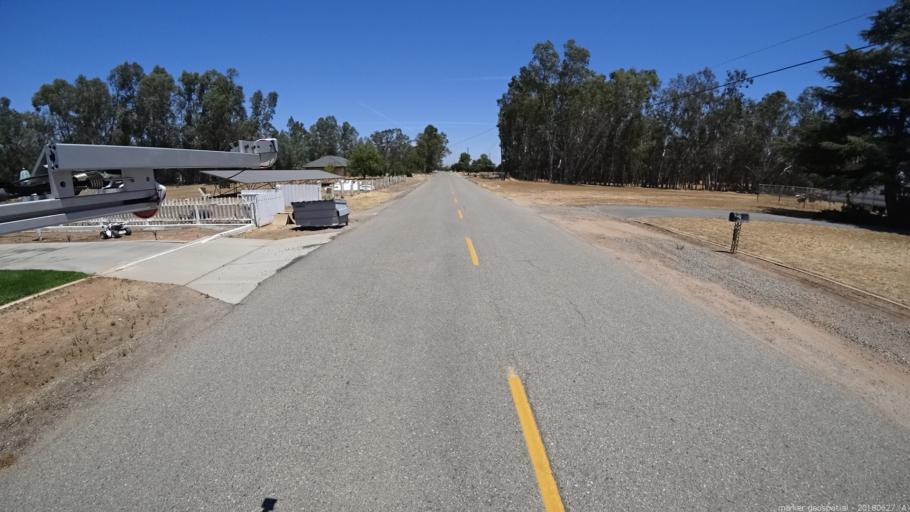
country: US
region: California
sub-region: Madera County
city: Bonadelle Ranchos-Madera Ranchos
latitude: 36.9303
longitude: -119.8654
